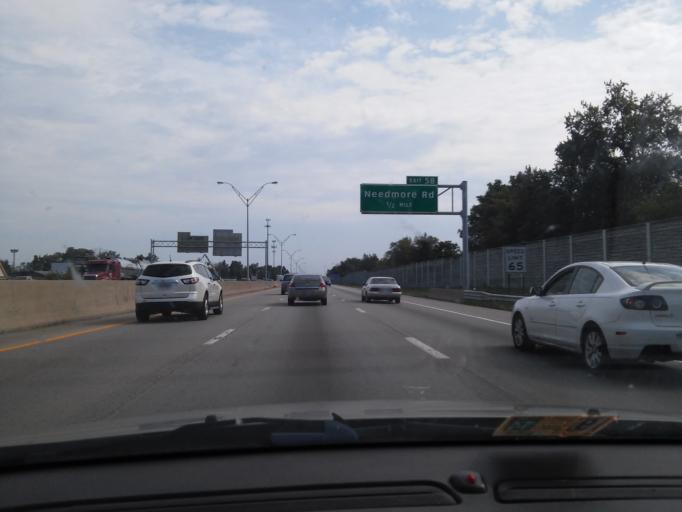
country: US
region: Ohio
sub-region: Montgomery County
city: Northridge
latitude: 39.8296
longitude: -84.1895
